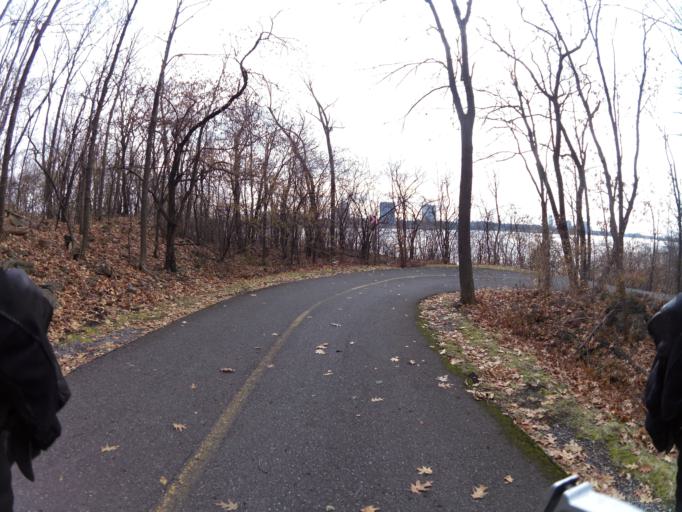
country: CA
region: Ontario
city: Ottawa
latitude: 45.4184
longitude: -75.7391
